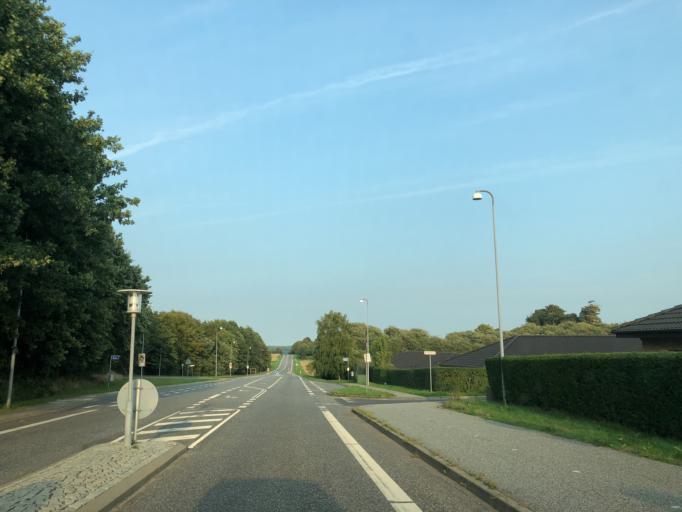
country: DK
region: South Denmark
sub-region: Vejle Kommune
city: Jelling
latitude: 55.7012
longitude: 9.3883
